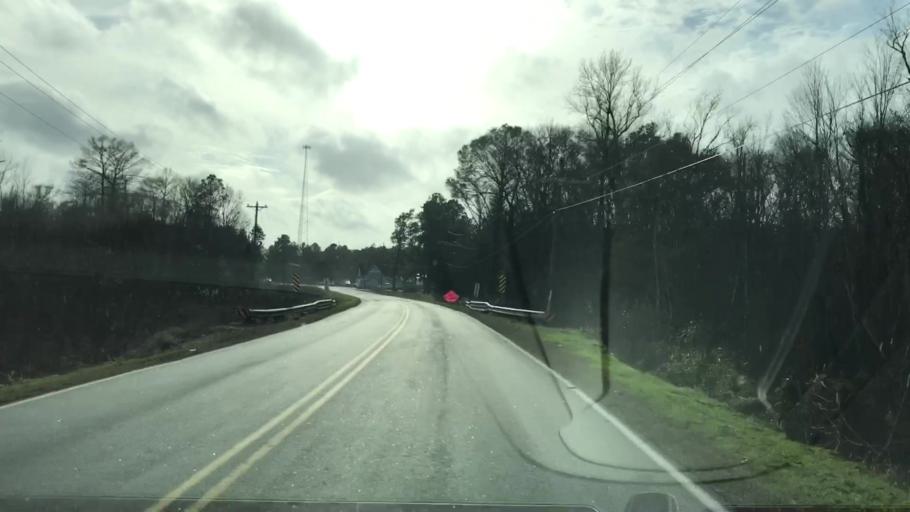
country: US
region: South Carolina
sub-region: Williamsburg County
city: Andrews
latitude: 33.3601
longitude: -79.6542
